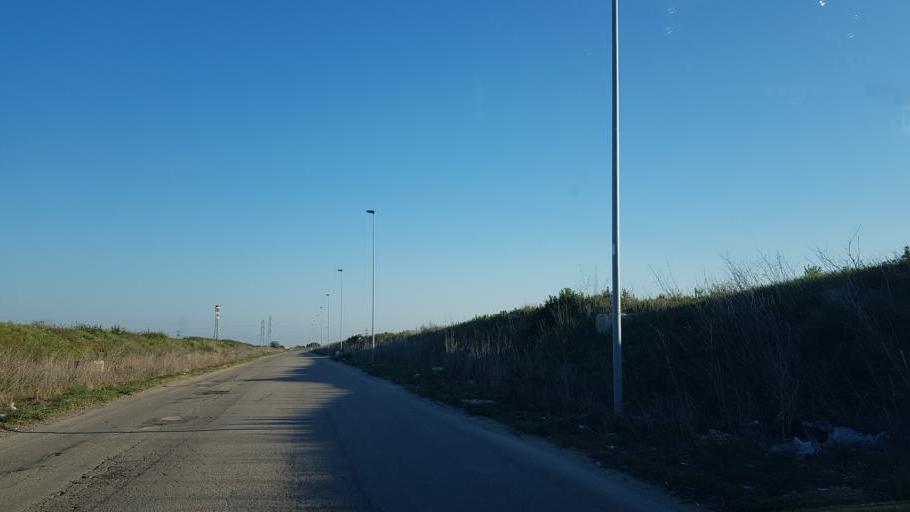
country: IT
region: Apulia
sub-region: Provincia di Brindisi
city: La Rosa
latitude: 40.6215
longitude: 17.9700
